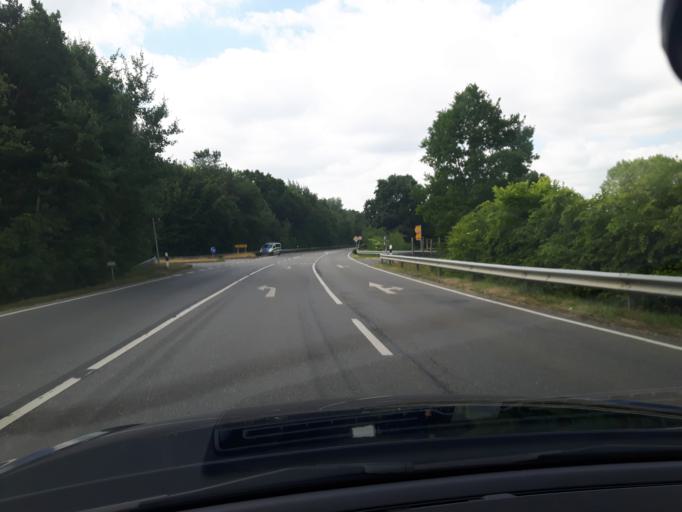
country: DE
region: Schleswig-Holstein
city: Sierksdorf
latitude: 54.0698
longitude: 10.7709
